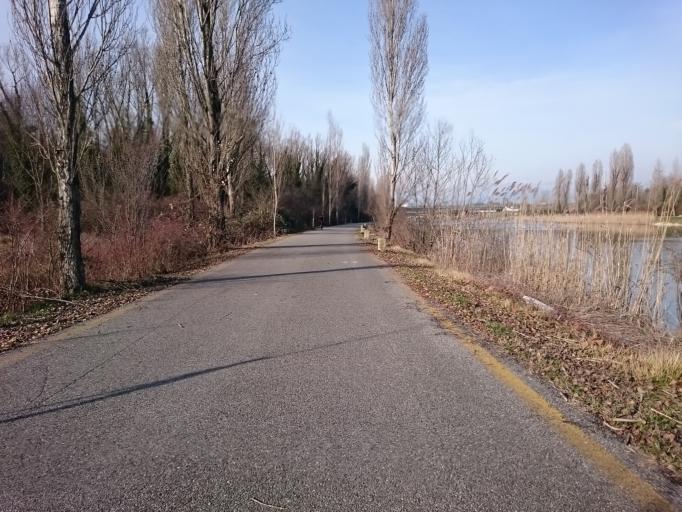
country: IT
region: Lombardy
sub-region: Provincia di Mantova
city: Ponti sul Mincio
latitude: 45.4244
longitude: 10.7000
